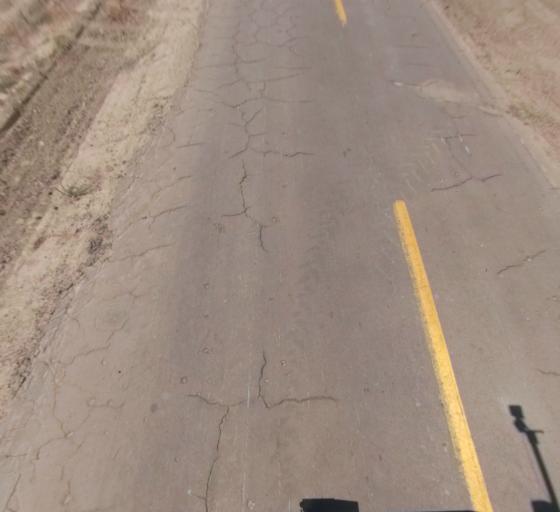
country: US
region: California
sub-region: Fresno County
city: Biola
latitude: 36.8707
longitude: -119.9294
